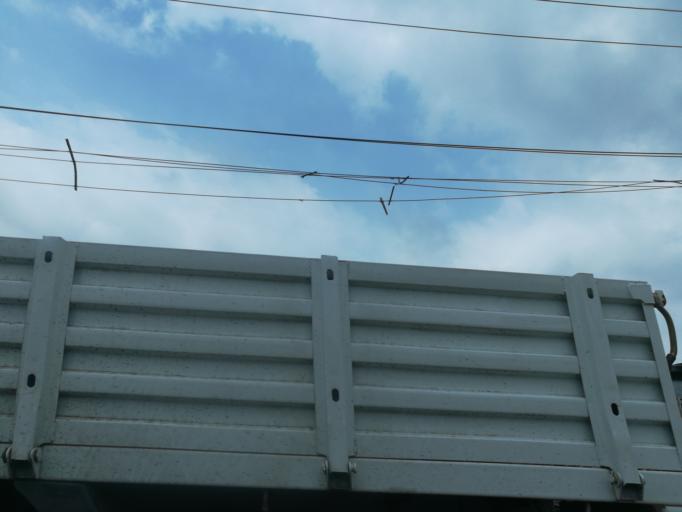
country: NG
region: Lagos
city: Lagos
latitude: 6.4553
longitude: 3.4040
